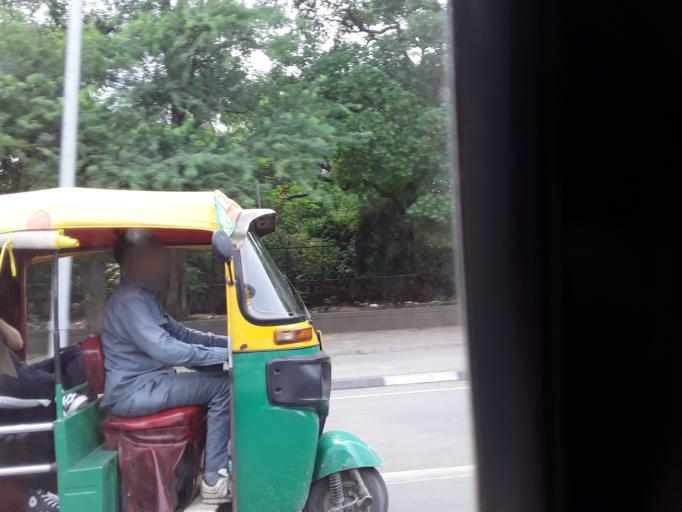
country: IN
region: NCT
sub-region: New Delhi
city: New Delhi
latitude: 28.5493
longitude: 77.2284
